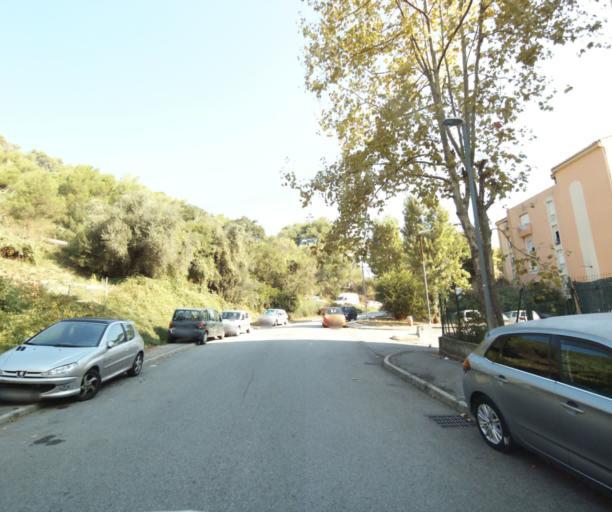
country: FR
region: Provence-Alpes-Cote d'Azur
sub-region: Departement des Alpes-Maritimes
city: Cantaron
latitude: 43.7709
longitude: 7.3310
